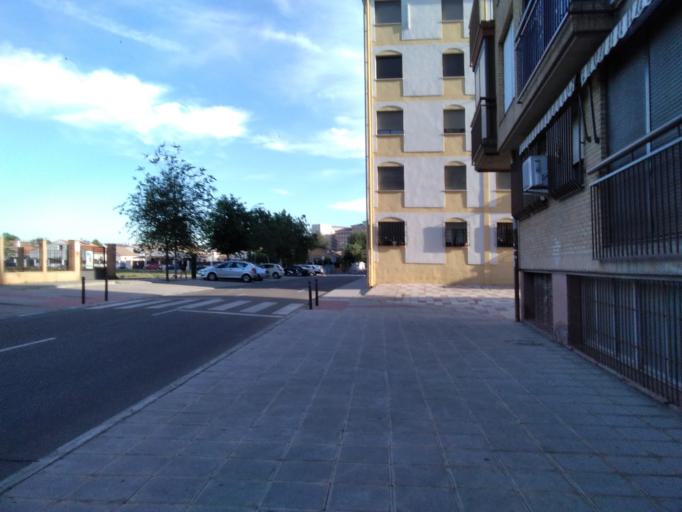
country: ES
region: Castille-La Mancha
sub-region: Province of Toledo
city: Toledo
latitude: 39.8673
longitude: -4.0329
